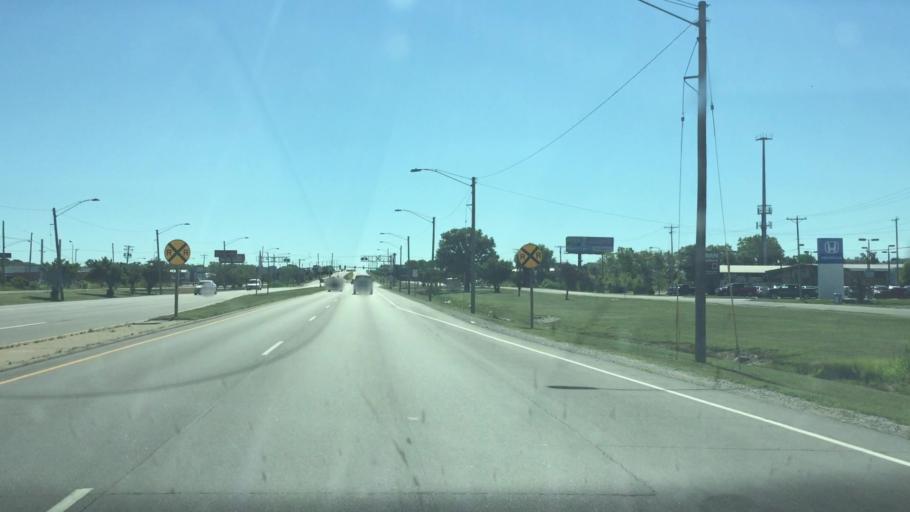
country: US
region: Wisconsin
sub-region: Outagamie County
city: Appleton
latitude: 44.2617
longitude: -88.4454
